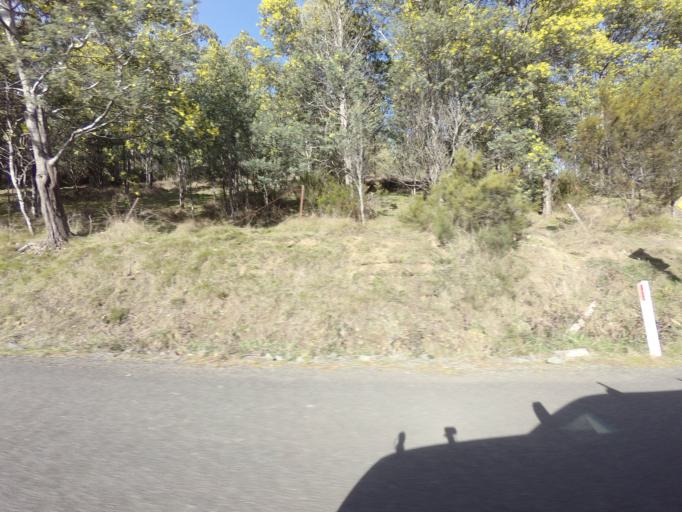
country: AU
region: Tasmania
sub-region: Huon Valley
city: Cygnet
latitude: -43.1758
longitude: 147.1516
